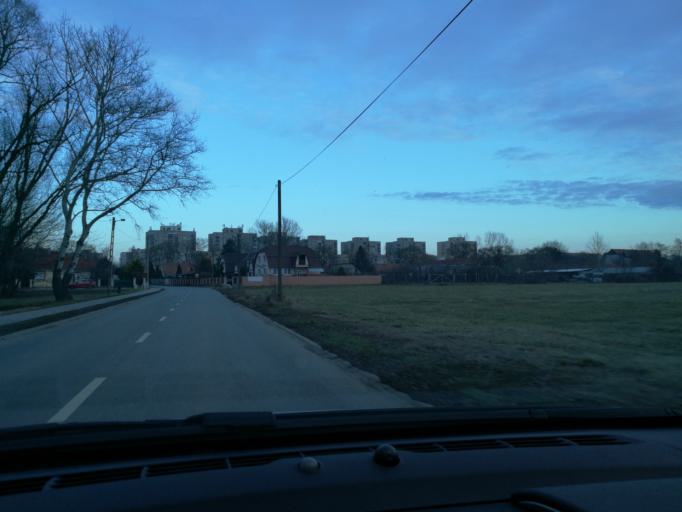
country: HU
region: Szabolcs-Szatmar-Bereg
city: Nyiregyhaza
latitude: 47.9592
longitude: 21.7327
